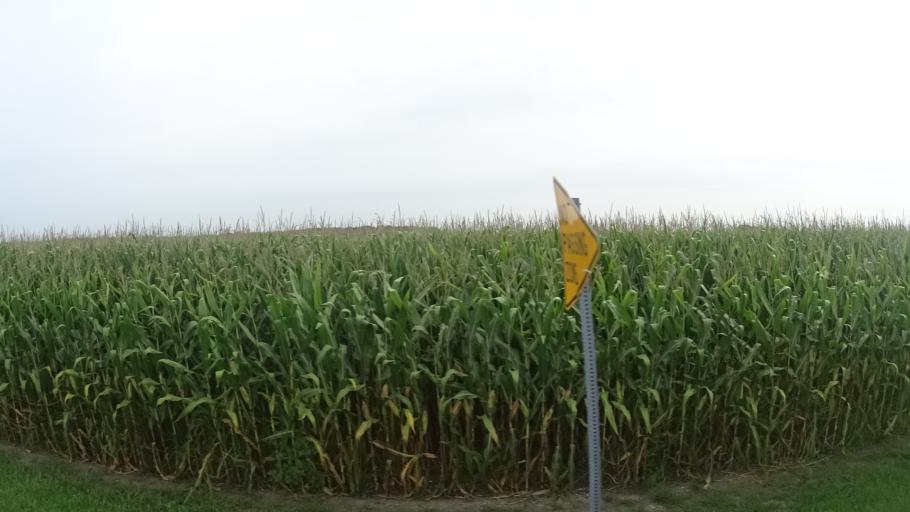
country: US
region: Indiana
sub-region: Madison County
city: Pendleton
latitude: 40.0077
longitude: -85.7843
